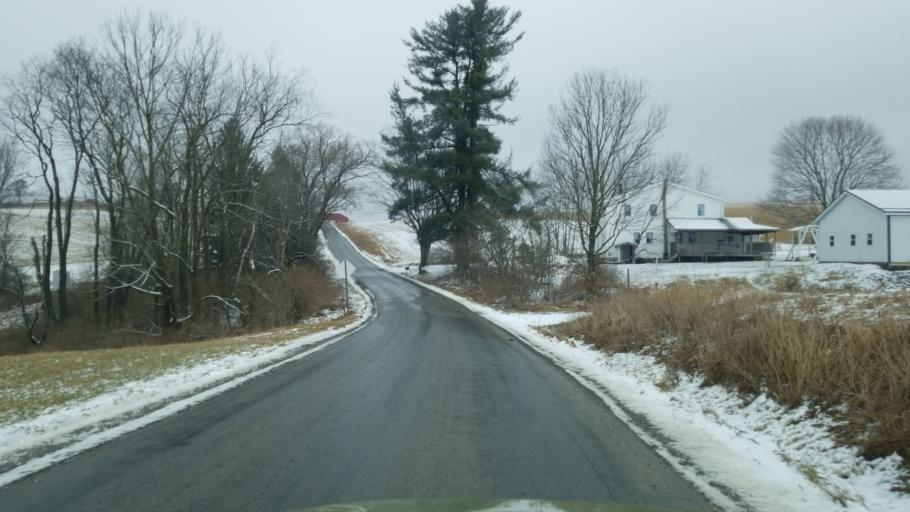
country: US
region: Pennsylvania
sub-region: Jefferson County
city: Sykesville
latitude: 41.0386
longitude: -78.7822
